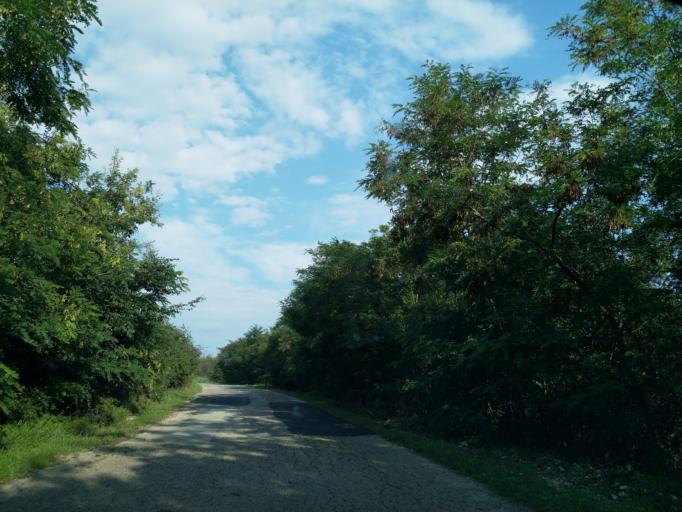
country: RS
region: Central Serbia
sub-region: Pomoravski Okrug
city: Jagodina
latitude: 43.9946
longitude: 21.1965
